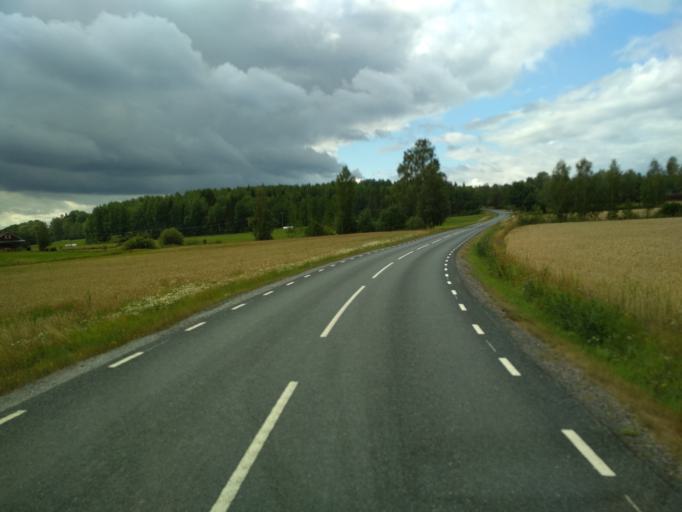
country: SE
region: Soedermanland
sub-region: Eskilstuna Kommun
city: Arla
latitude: 59.1883
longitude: 16.6268
